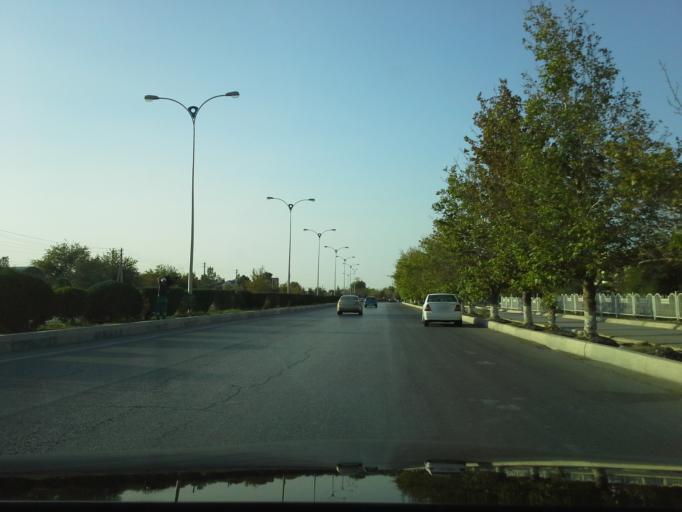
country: TM
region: Ahal
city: Abadan
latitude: 38.0333
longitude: 58.1908
